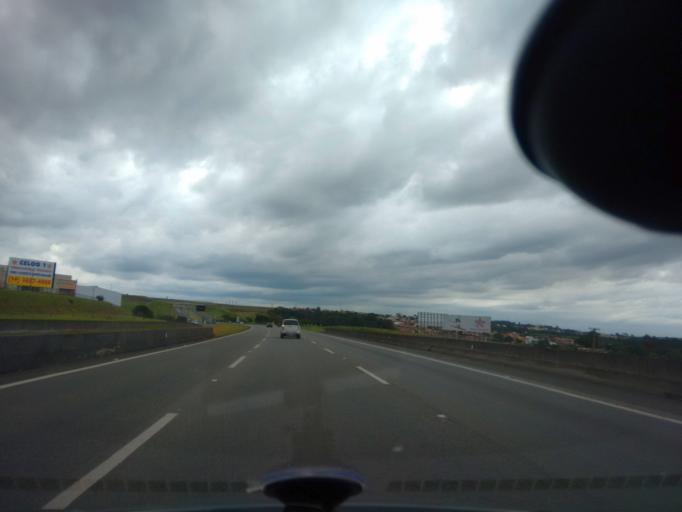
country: BR
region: Sao Paulo
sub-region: Hortolandia
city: Hortolandia
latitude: -22.9003
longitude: -47.2094
